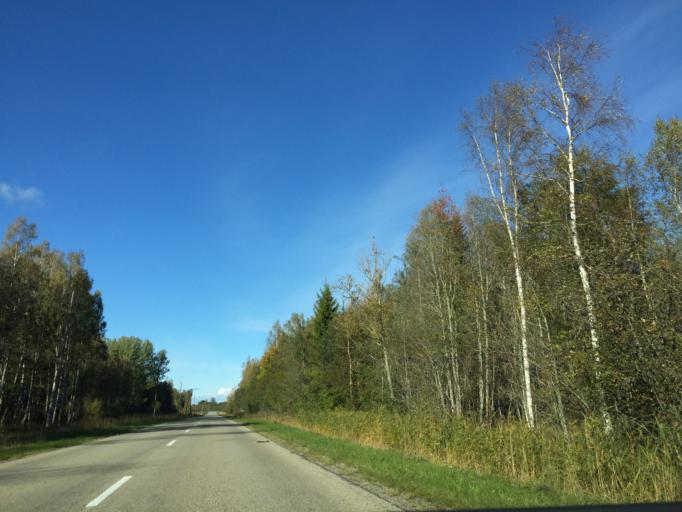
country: LV
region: Rojas
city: Roja
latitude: 57.4391
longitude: 22.9058
